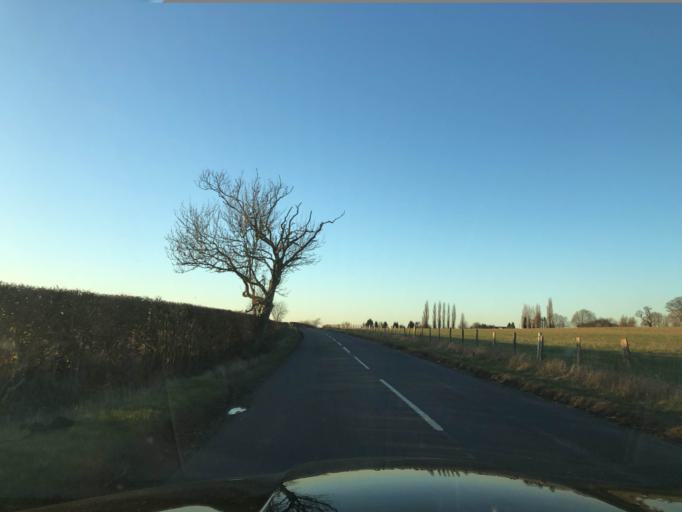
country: GB
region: England
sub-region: Warwickshire
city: Harbury
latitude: 52.2304
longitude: -1.4745
